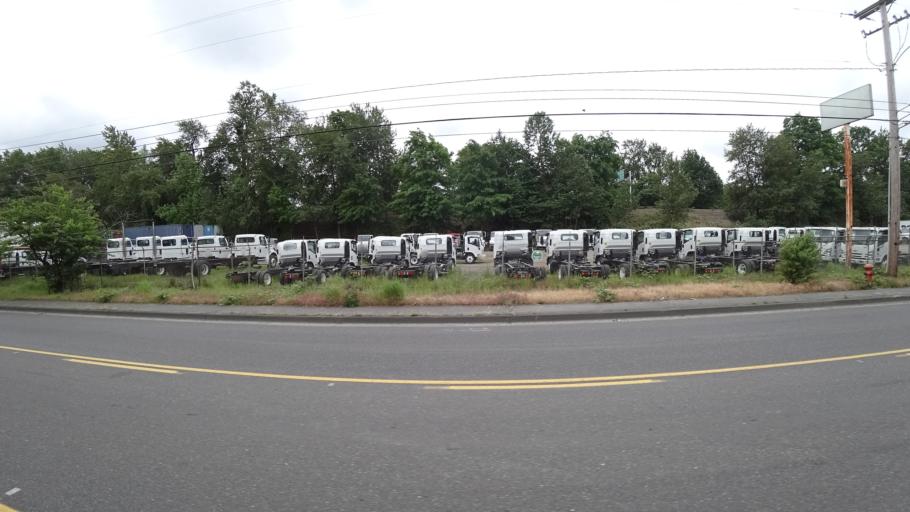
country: US
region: Washington
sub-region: Clark County
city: Vancouver
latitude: 45.6001
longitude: -122.6745
